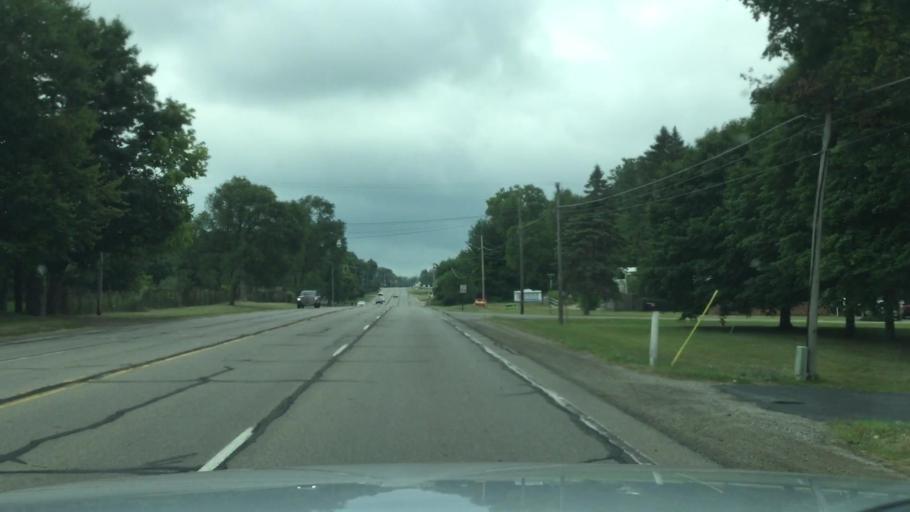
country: US
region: Michigan
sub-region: Genesee County
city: Burton
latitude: 43.0333
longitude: -83.6057
